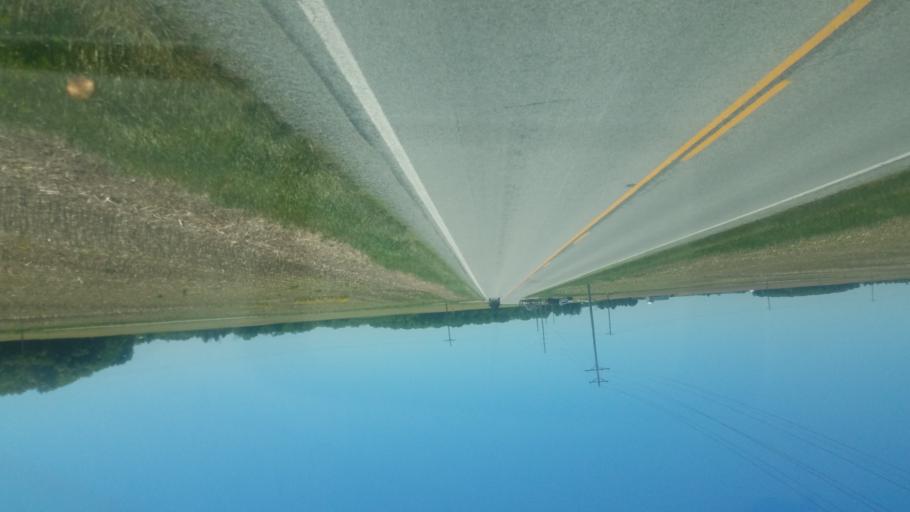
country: US
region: Ohio
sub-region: Miami County
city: Piqua
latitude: 40.2141
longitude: -84.3071
